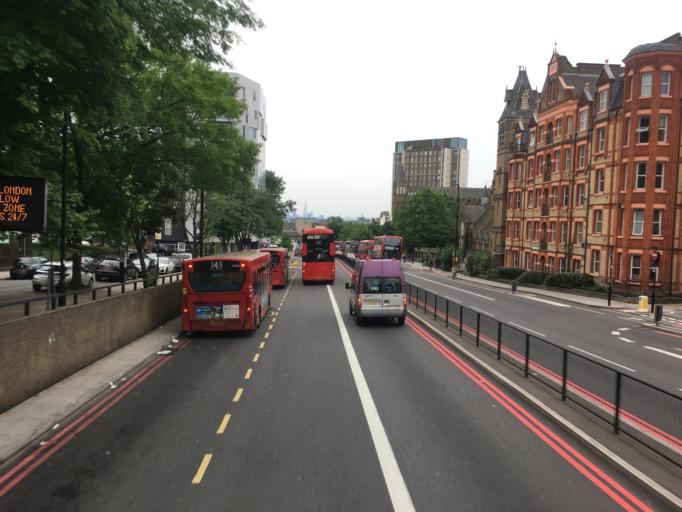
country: GB
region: England
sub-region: Greater London
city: Crouch End
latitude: 51.5683
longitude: -0.1362
